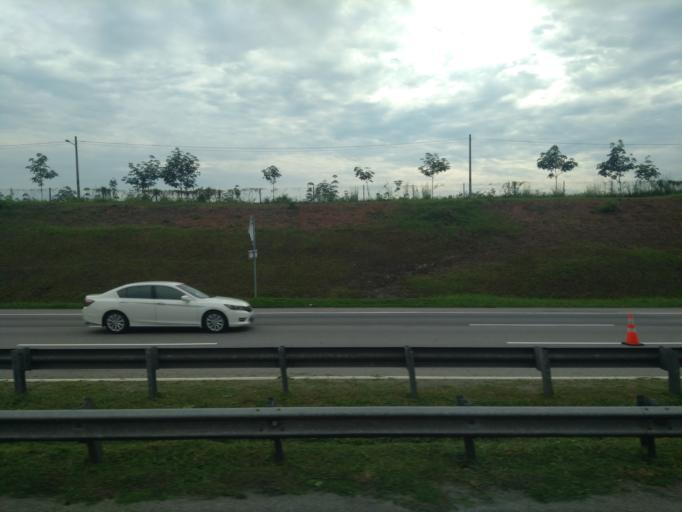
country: MY
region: Melaka
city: Alor Gajah
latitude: 2.4192
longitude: 102.2159
